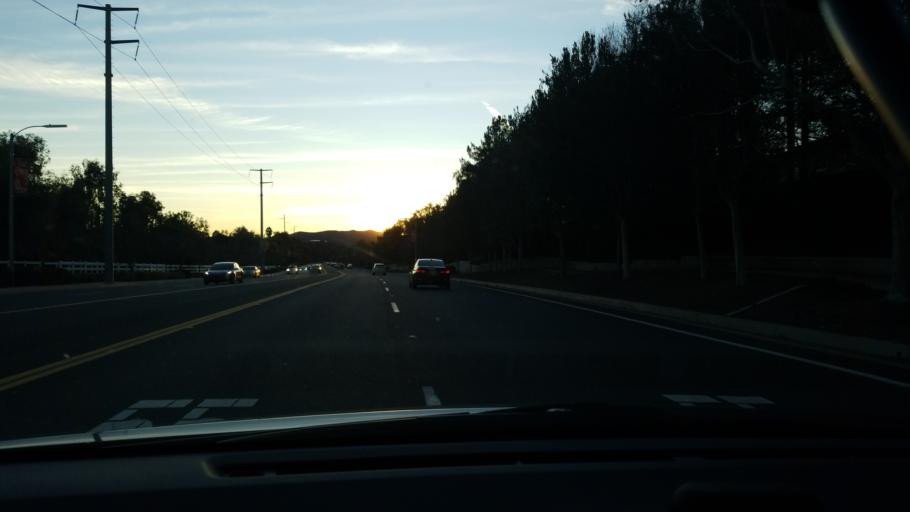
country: US
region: California
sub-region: Riverside County
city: Temecula
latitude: 33.5136
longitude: -117.1062
